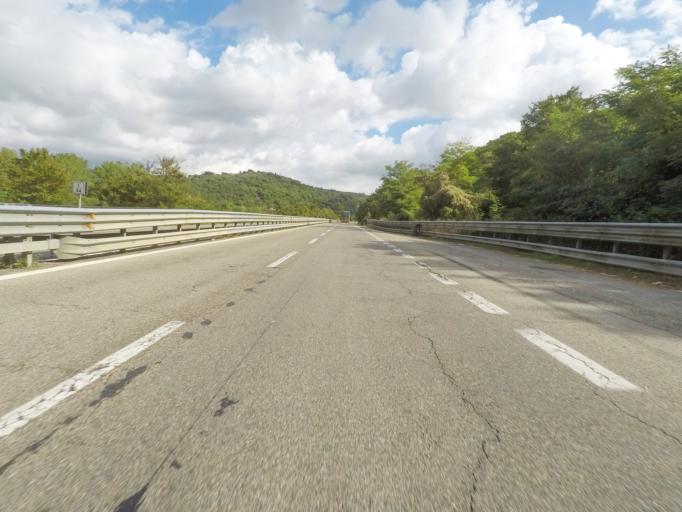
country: IT
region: Tuscany
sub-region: Province of Arezzo
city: Lucignano
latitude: 43.2544
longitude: 11.6868
